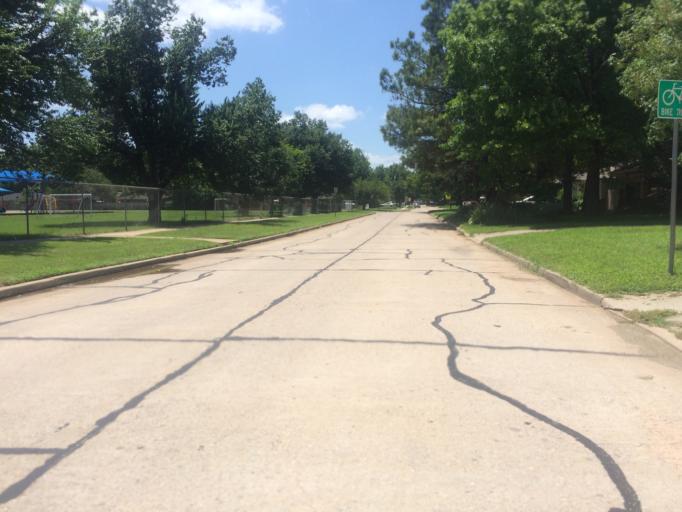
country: US
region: Oklahoma
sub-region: Cleveland County
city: Norman
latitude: 35.2143
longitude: -97.4638
